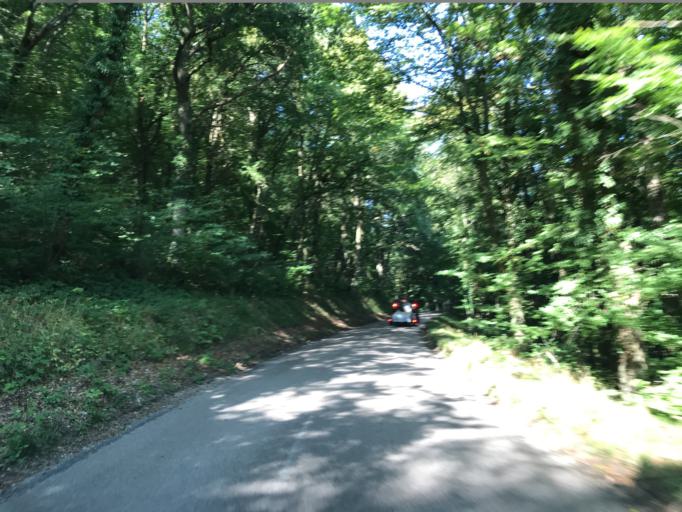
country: FR
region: Haute-Normandie
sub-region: Departement de l'Eure
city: Heudreville-sur-Eure
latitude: 49.1092
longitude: 1.2104
